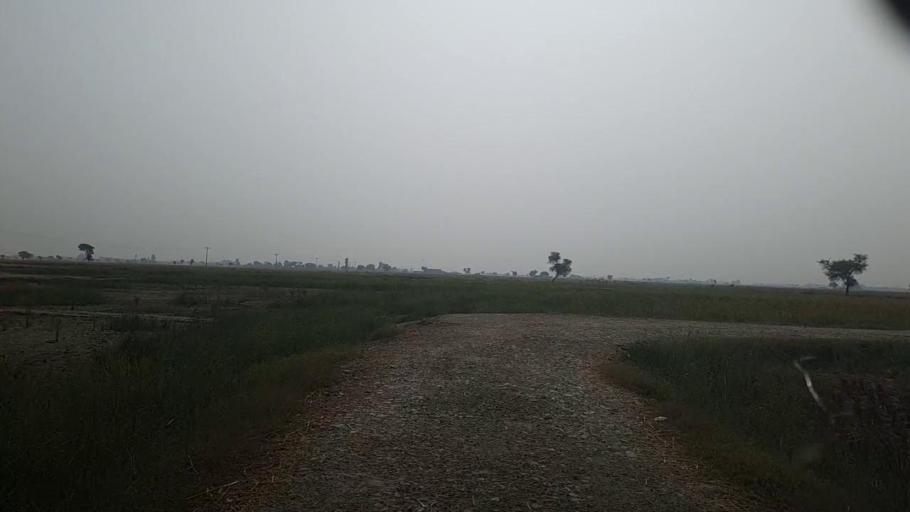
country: PK
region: Sindh
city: Kashmor
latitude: 28.3870
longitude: 69.4278
